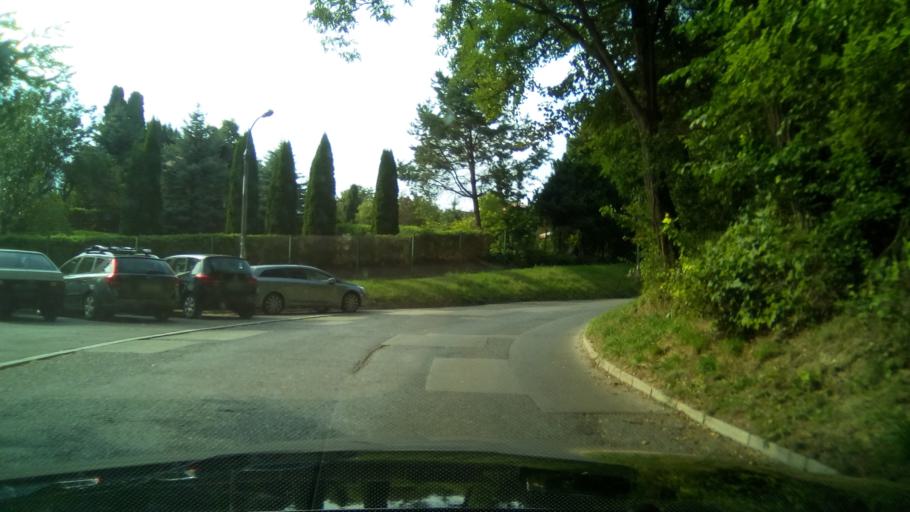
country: PL
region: Lesser Poland Voivodeship
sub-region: Krakow
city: Krakow
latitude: 50.0510
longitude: 19.9018
